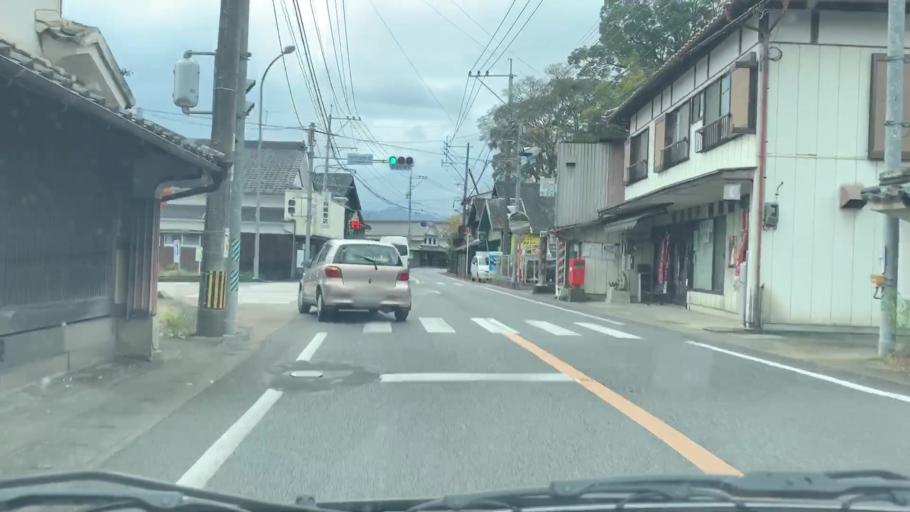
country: JP
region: Saga Prefecture
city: Kashima
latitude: 33.1371
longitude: 130.0636
